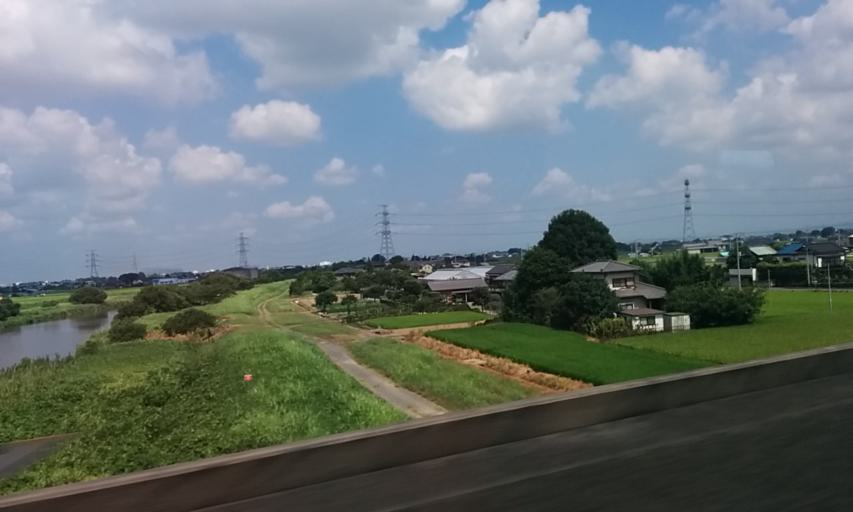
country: JP
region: Saitama
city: Kurihashi
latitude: 36.0995
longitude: 139.6989
